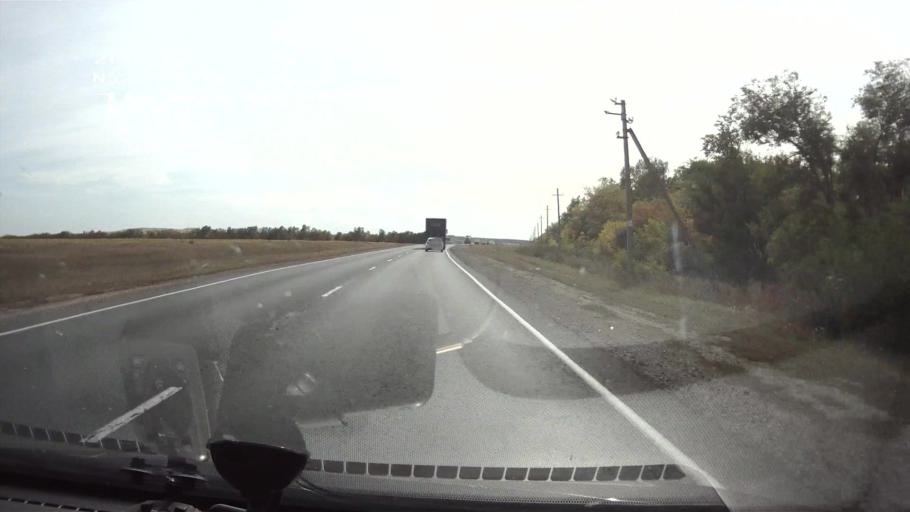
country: RU
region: Saratov
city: Alekseyevka
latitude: 52.2712
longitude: 47.9292
